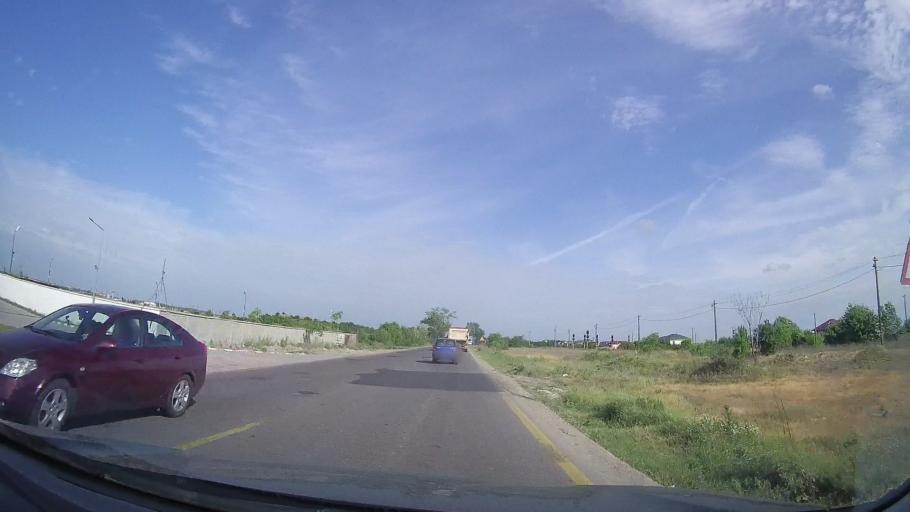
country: RO
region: Ilfov
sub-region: Comuna Magurele
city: Varteju
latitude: 44.3715
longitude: 26.0104
